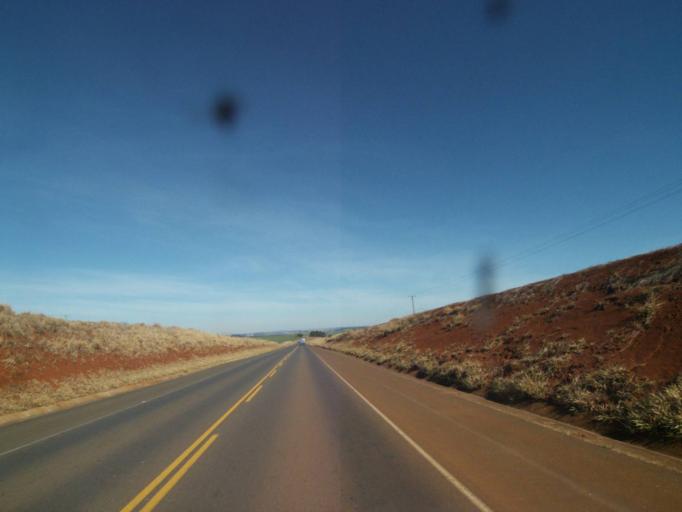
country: BR
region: Parana
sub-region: Tibagi
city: Tibagi
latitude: -24.4495
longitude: -50.4235
